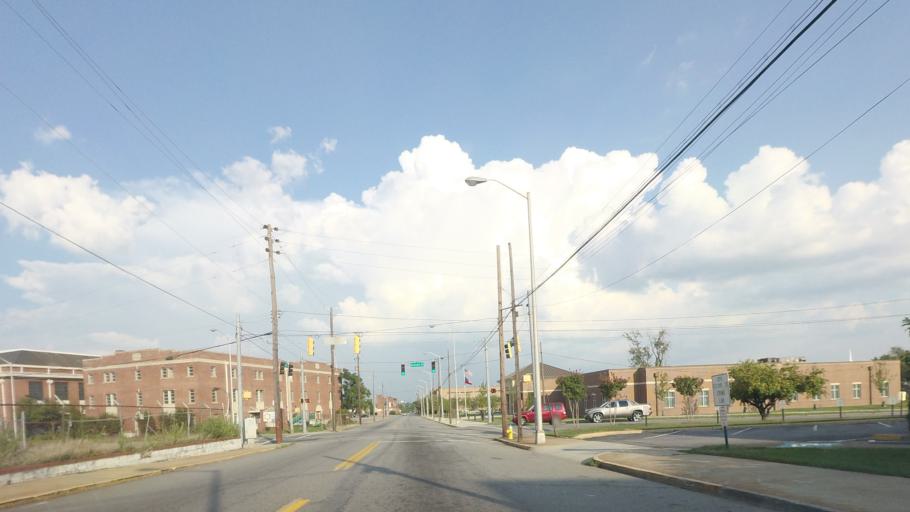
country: US
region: Georgia
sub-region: Bibb County
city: Macon
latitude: 32.8294
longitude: -83.6355
